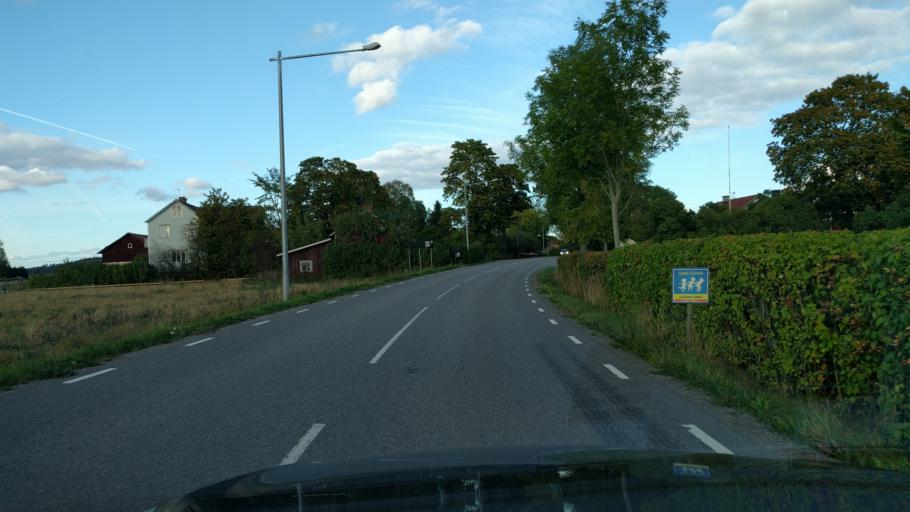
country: SE
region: Uppsala
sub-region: Osthammars Kommun
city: Bjorklinge
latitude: 60.1548
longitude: 17.5909
